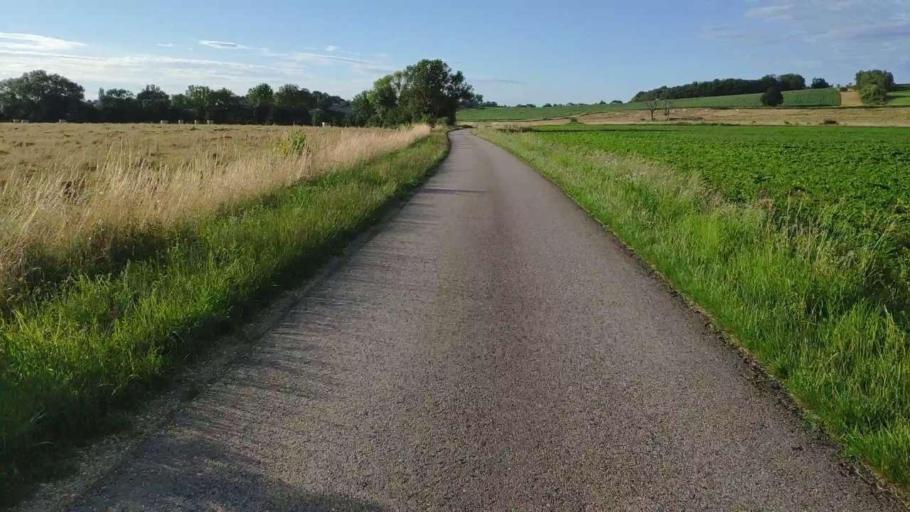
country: FR
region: Franche-Comte
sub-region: Departement du Jura
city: Bletterans
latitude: 46.7744
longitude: 5.4963
